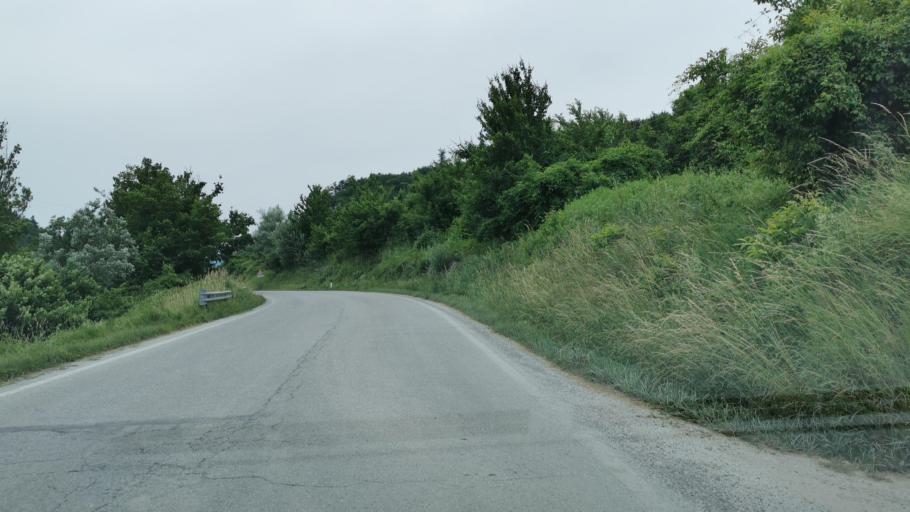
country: IT
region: Piedmont
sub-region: Provincia di Cuneo
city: Torresina
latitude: 44.4120
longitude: 8.0478
